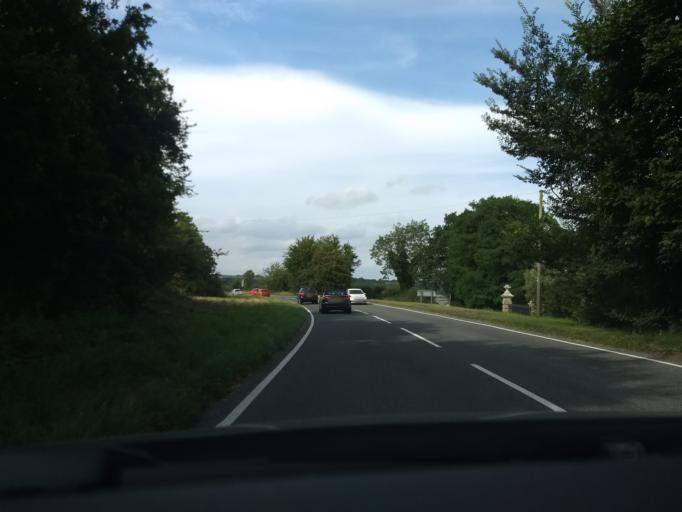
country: GB
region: England
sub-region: Suffolk
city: Ipswich
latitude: 52.0152
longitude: 1.1677
